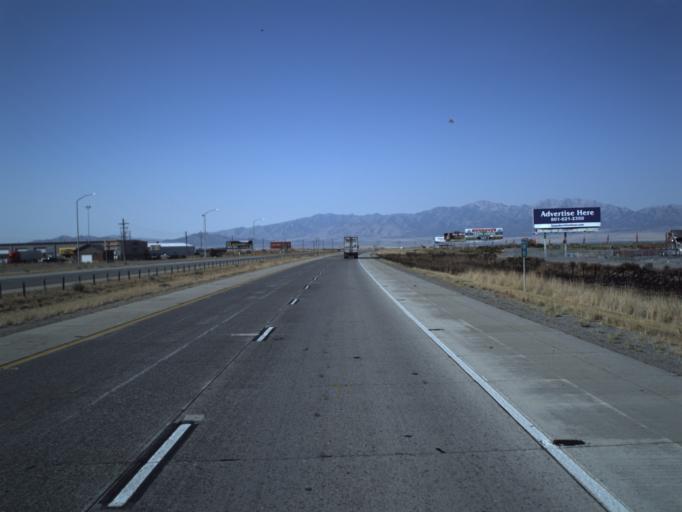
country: US
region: Utah
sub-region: Tooele County
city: Stansbury park
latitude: 40.6864
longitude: -112.2710
